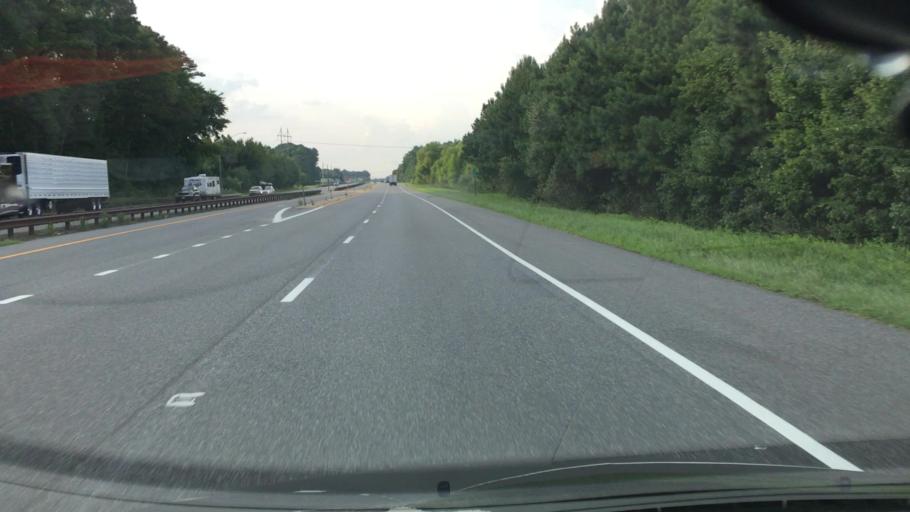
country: US
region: Delaware
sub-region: Sussex County
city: Selbyville
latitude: 38.4205
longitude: -75.2148
